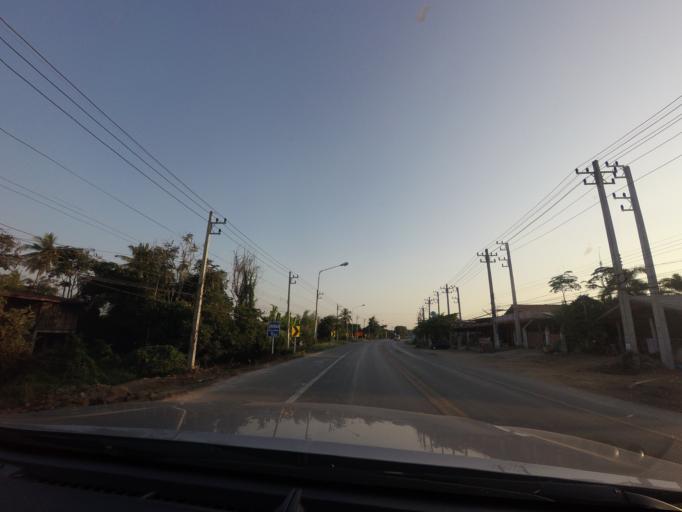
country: TH
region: Sukhothai
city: Si Samrong
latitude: 17.2075
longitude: 99.8677
